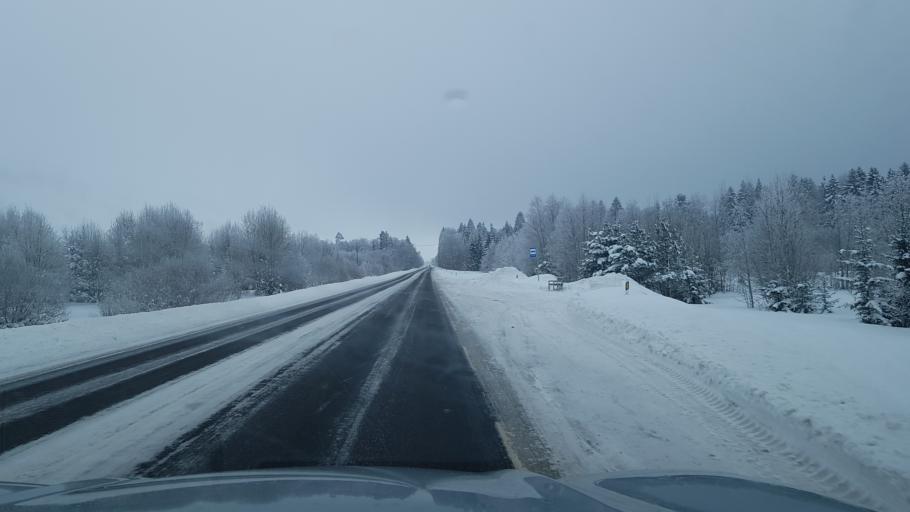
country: EE
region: Ida-Virumaa
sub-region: Johvi vald
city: Johvi
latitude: 59.2841
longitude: 27.3964
